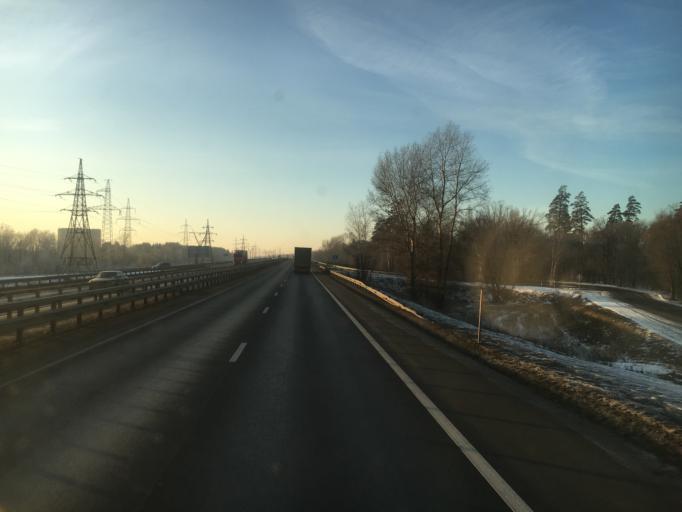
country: RU
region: Samara
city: Pribrezhnyy
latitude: 53.5173
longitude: 49.8416
